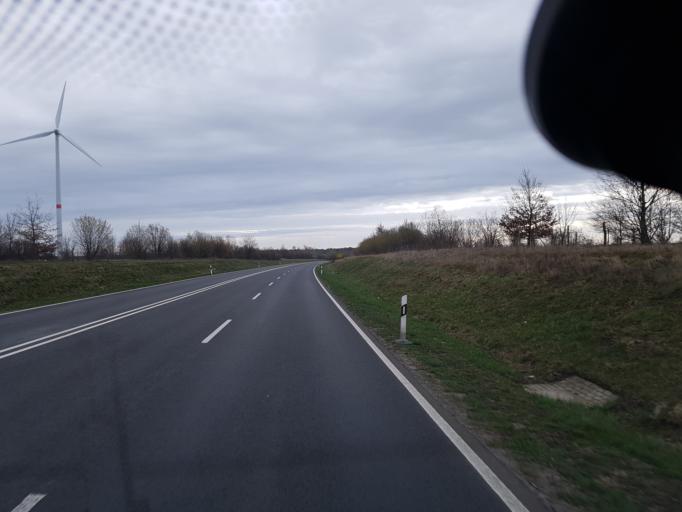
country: DE
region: Brandenburg
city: Beeskow
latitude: 52.1999
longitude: 14.2413
